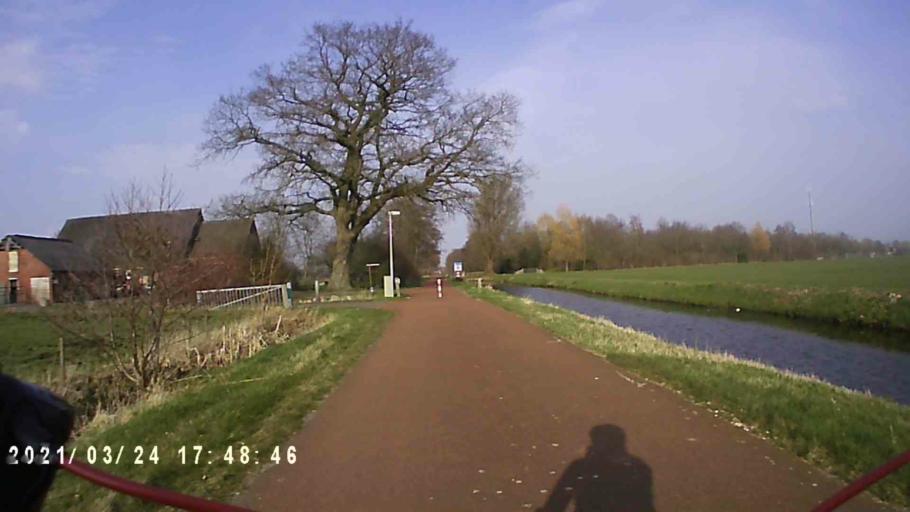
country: NL
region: Groningen
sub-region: Gemeente Leek
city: Leek
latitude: 53.1191
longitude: 6.3379
